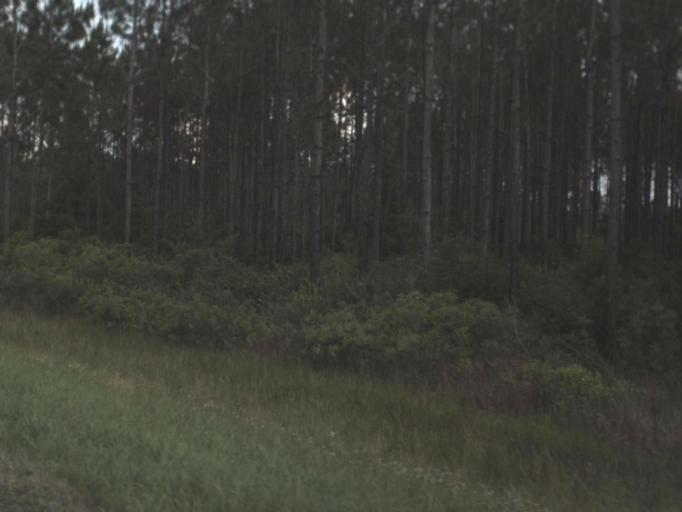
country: US
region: Florida
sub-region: Baker County
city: Macclenny
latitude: 30.5112
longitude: -82.2643
